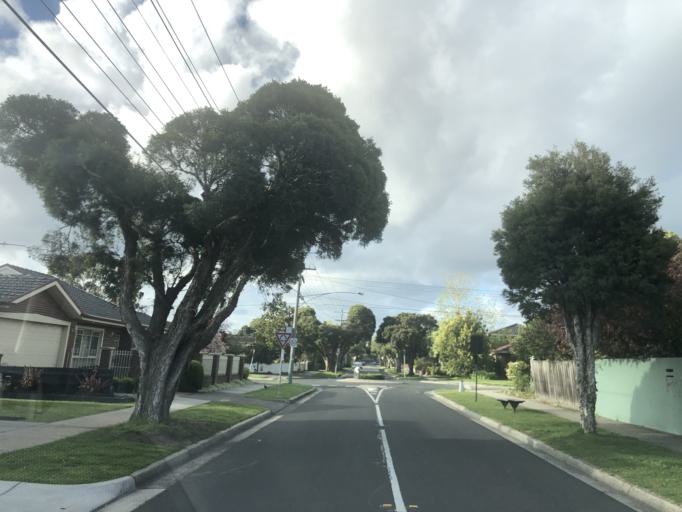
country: AU
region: Victoria
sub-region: Monash
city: Ashwood
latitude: -37.8805
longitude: 145.1244
